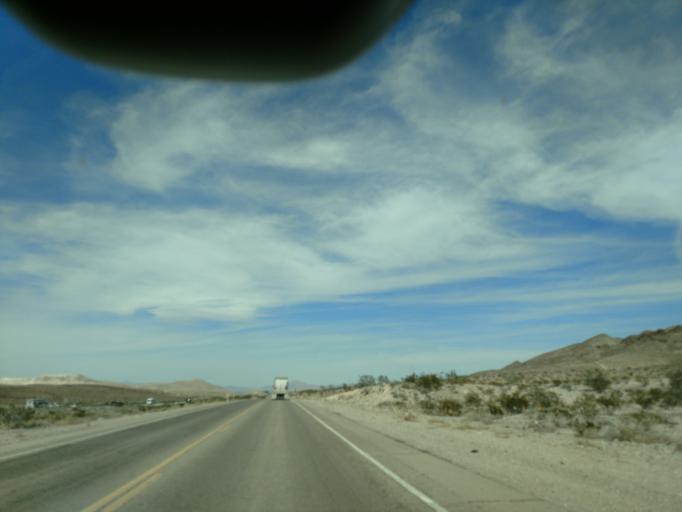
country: US
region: Nevada
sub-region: Clark County
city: Enterprise
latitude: 35.8857
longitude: -115.2240
